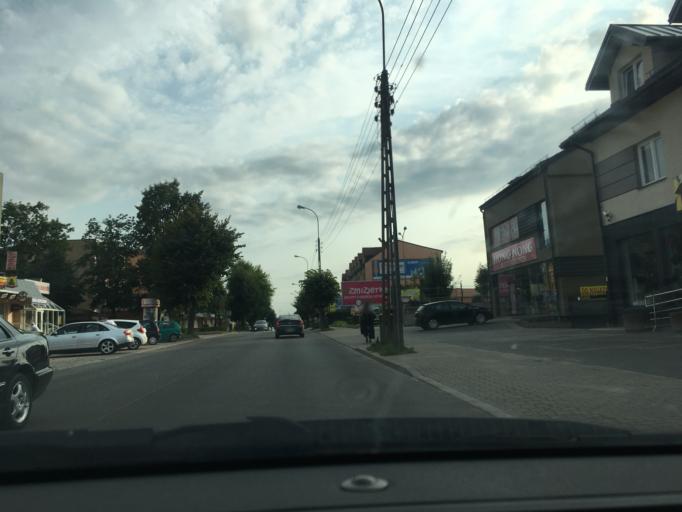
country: PL
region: Podlasie
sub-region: Powiat augustowski
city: Augustow
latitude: 53.8399
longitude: 22.9751
